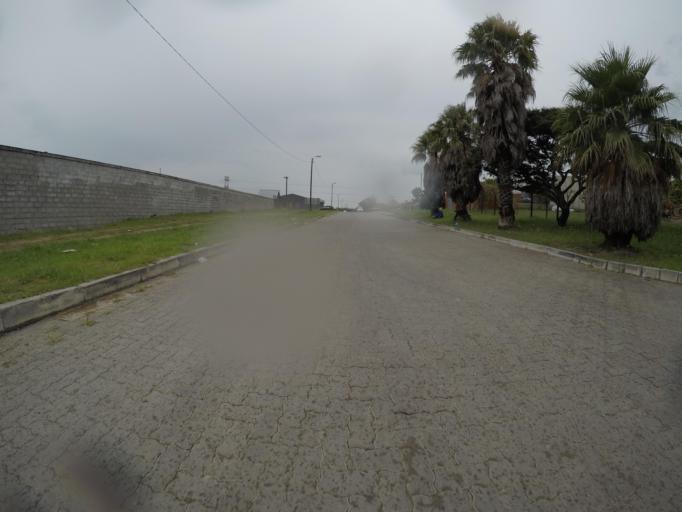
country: ZA
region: Eastern Cape
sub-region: Buffalo City Metropolitan Municipality
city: East London
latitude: -32.9915
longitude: 27.8305
